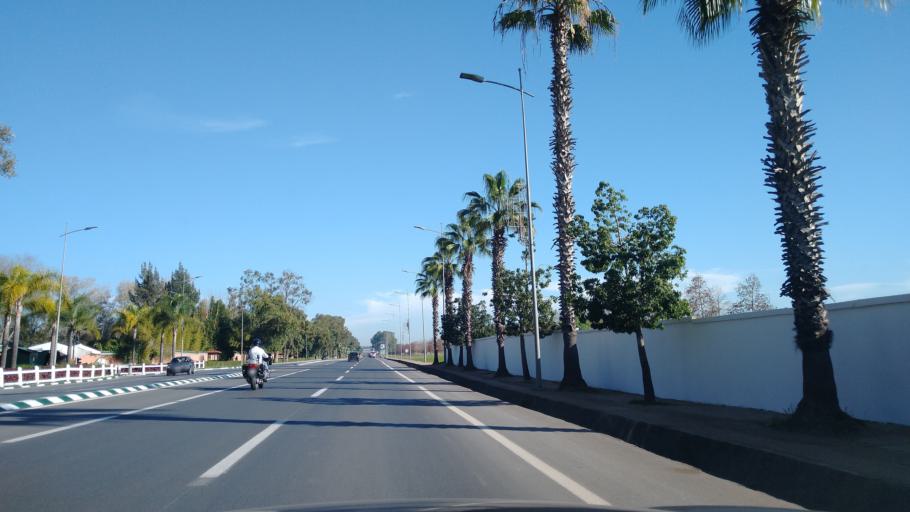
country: MA
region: Rabat-Sale-Zemmour-Zaer
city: Sale
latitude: 34.0298
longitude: -6.7436
